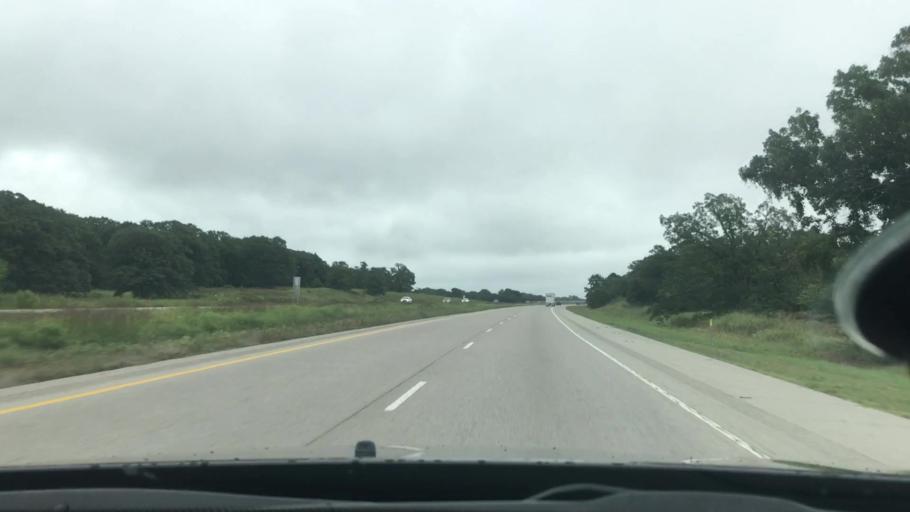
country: US
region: Oklahoma
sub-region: Okfuskee County
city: Okemah
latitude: 35.3992
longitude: -96.3890
